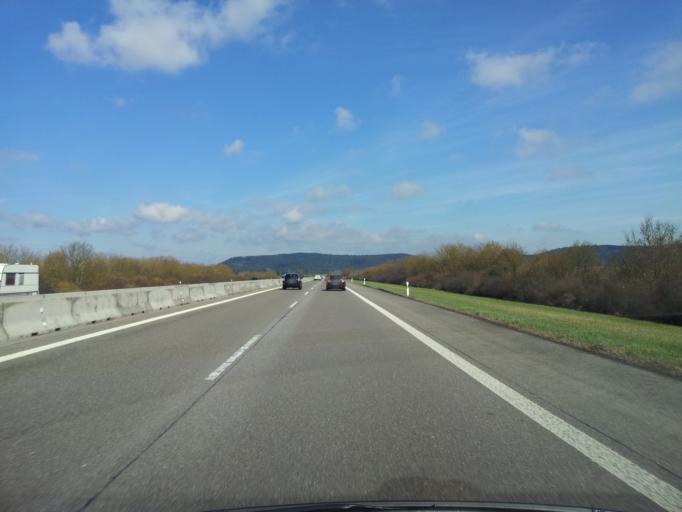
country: DE
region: Baden-Wuerttemberg
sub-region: Freiburg Region
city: Epfendorf
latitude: 48.2544
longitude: 8.6434
